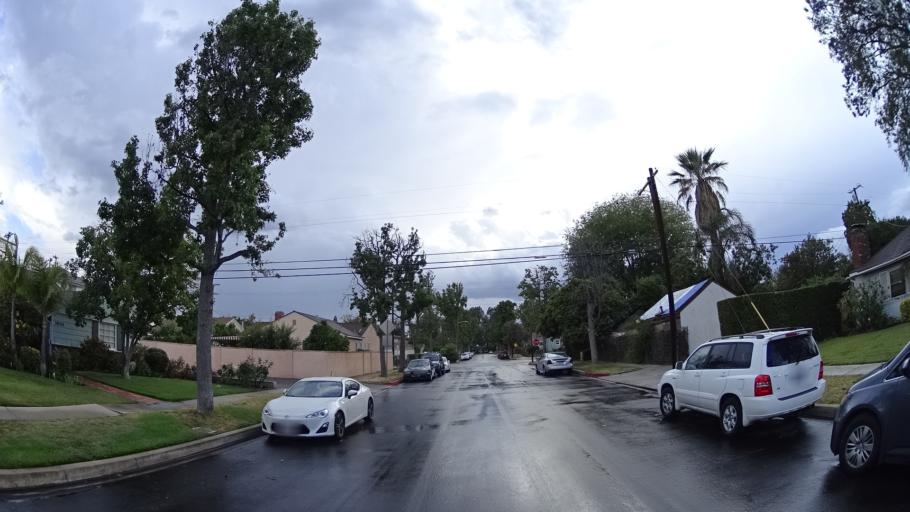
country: US
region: California
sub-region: Los Angeles County
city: Sherman Oaks
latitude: 34.1635
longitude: -118.4393
